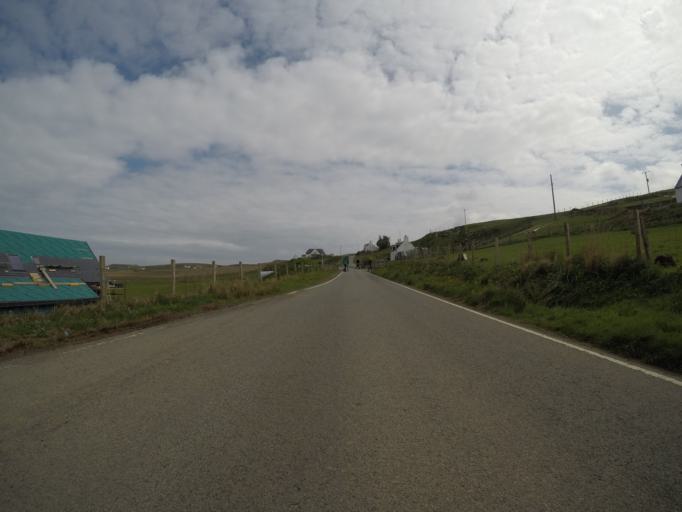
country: GB
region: Scotland
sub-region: Highland
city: Portree
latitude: 57.6842
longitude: -6.3040
